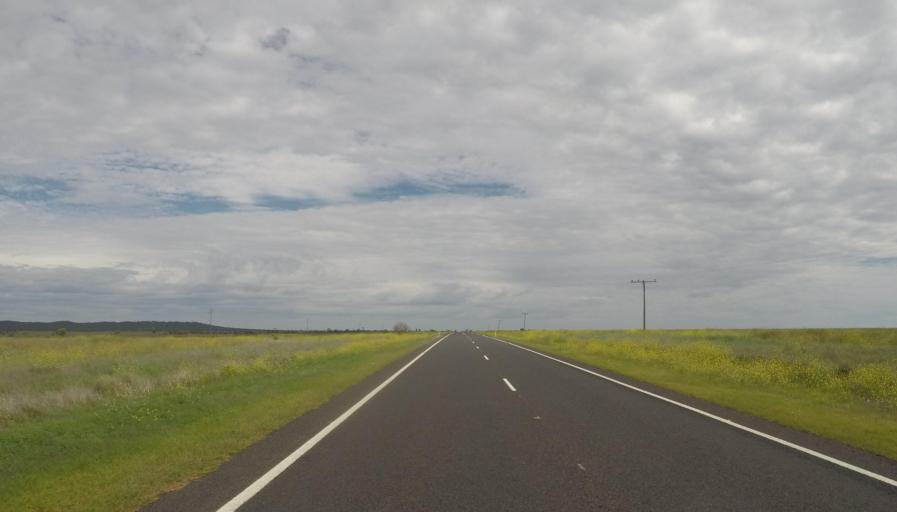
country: AU
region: Queensland
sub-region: Maranoa
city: Roma
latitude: -26.5842
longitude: 148.3304
